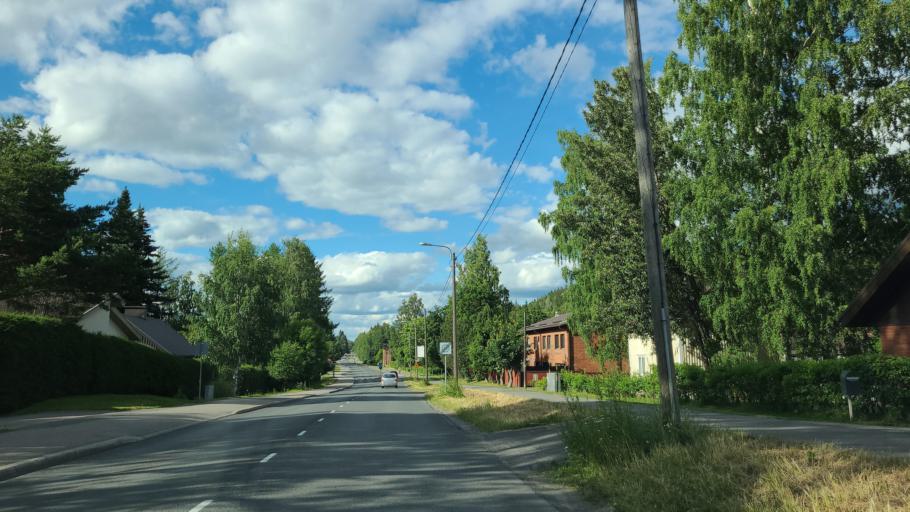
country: FI
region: Northern Savo
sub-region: Kuopio
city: Kuopio
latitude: 62.9265
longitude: 27.6326
